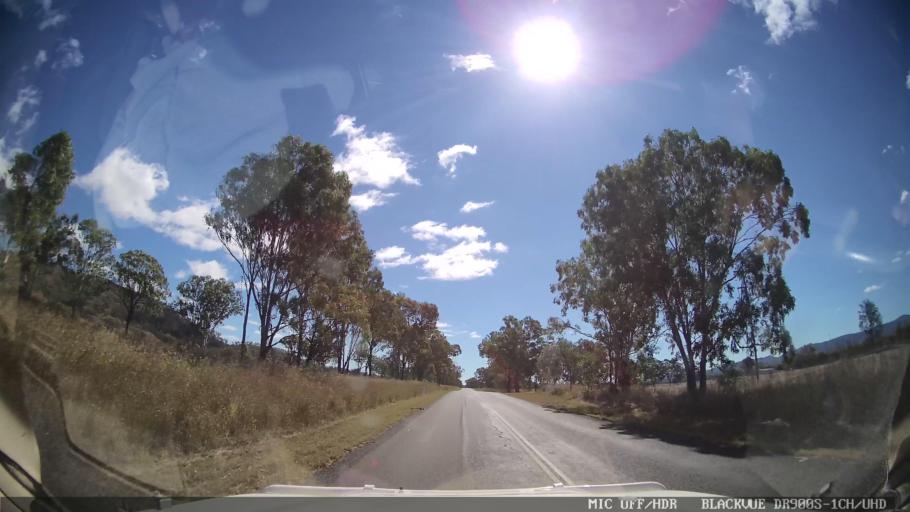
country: AU
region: Queensland
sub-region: Gladstone
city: Toolooa
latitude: -24.4534
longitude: 151.3466
